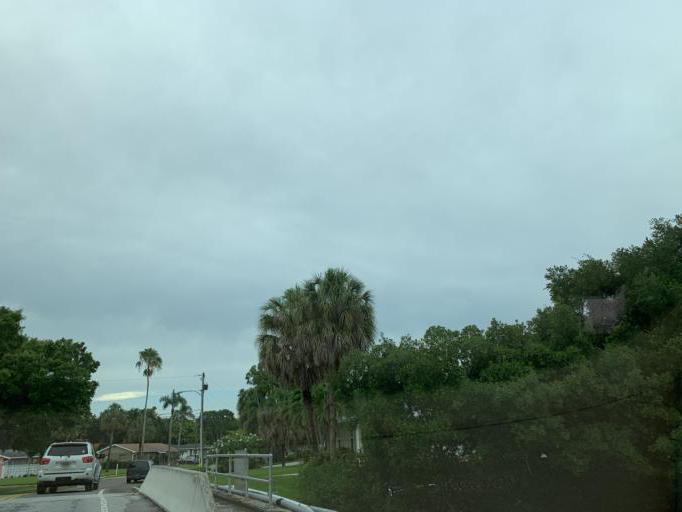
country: US
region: Florida
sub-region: Pinellas County
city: Gandy
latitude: 27.8208
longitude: -82.6062
